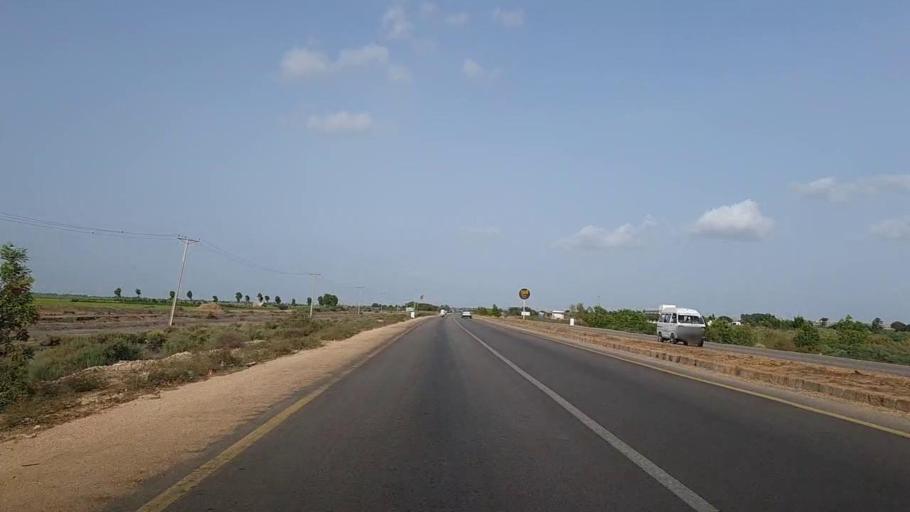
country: PK
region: Sindh
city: Thatta
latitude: 24.7451
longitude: 67.8539
